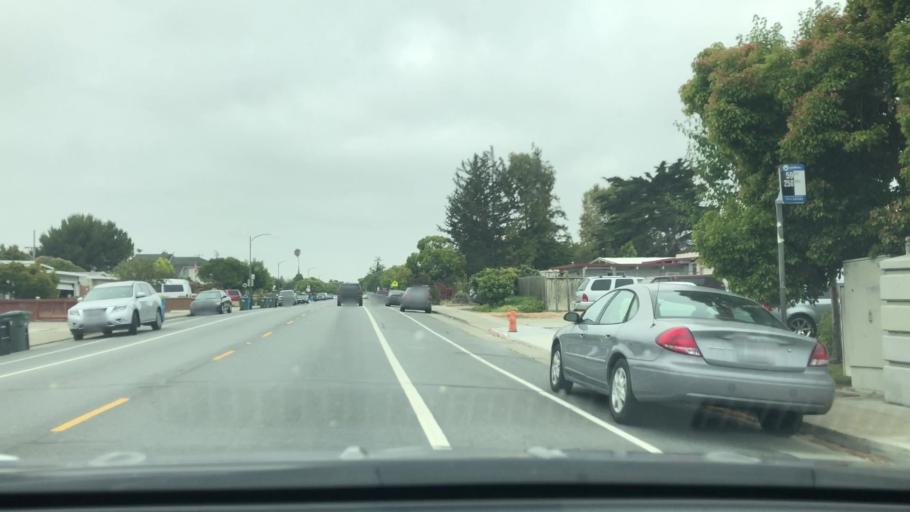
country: US
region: California
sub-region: San Mateo County
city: San Mateo
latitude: 37.5617
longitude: -122.2994
